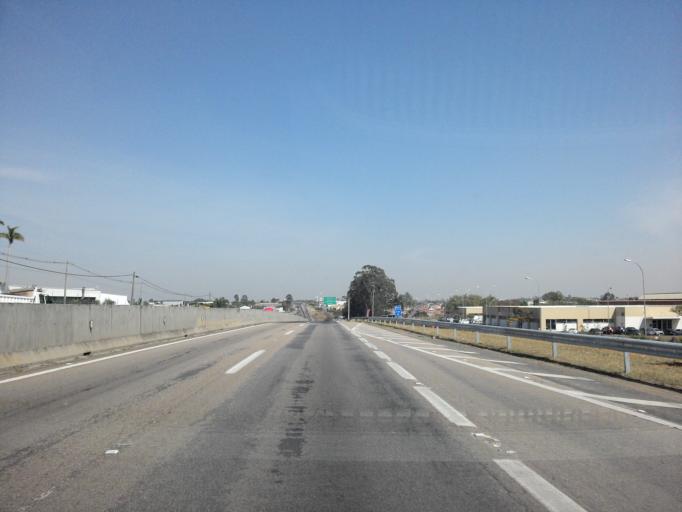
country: BR
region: Sao Paulo
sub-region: Hortolandia
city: Hortolandia
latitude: -22.9008
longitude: -47.1991
